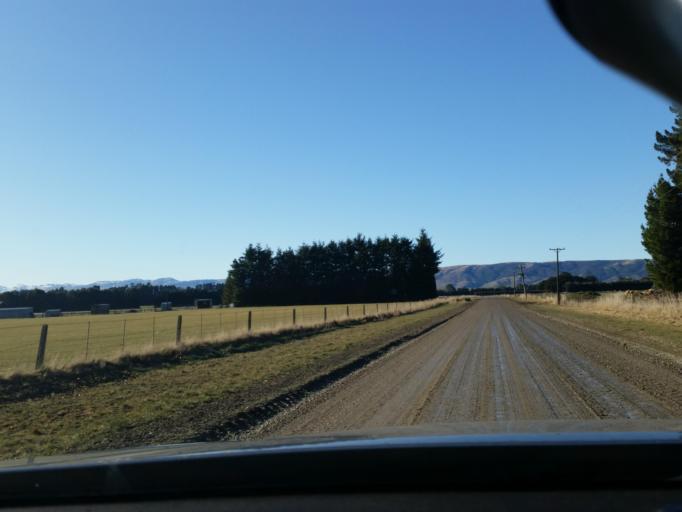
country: NZ
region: Otago
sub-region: Queenstown-Lakes District
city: Kingston
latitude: -45.7451
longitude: 168.7031
